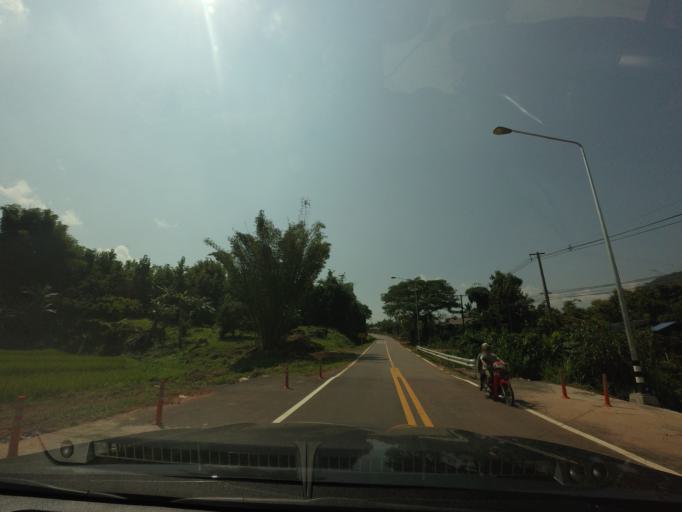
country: TH
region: Nan
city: Bo Kluea
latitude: 19.0985
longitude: 101.1544
